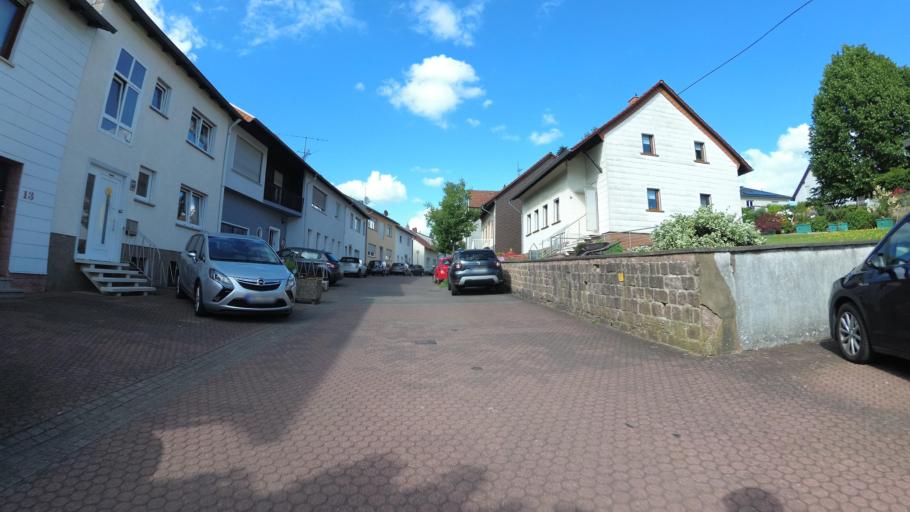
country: DE
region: Saarland
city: Heusweiler
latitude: 49.3388
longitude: 6.9339
